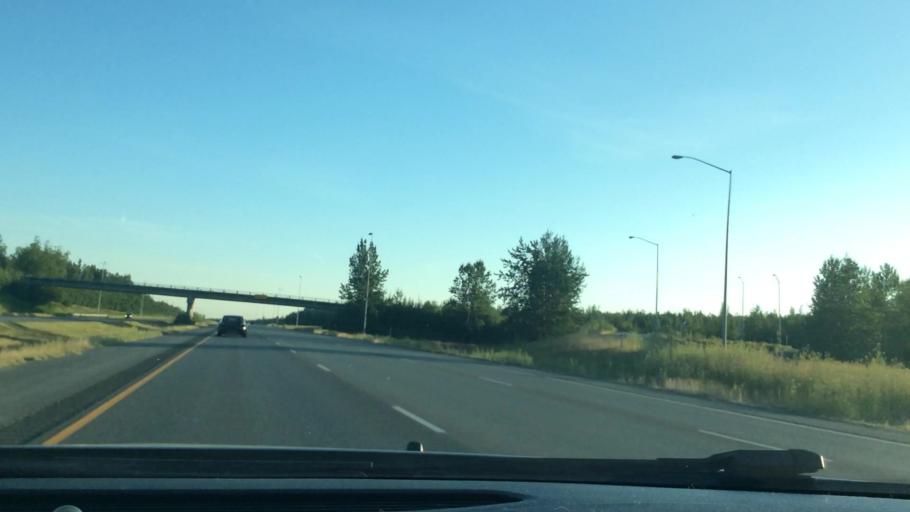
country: US
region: Alaska
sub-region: Anchorage Municipality
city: Elmendorf Air Force Base
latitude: 61.2547
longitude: -149.6564
